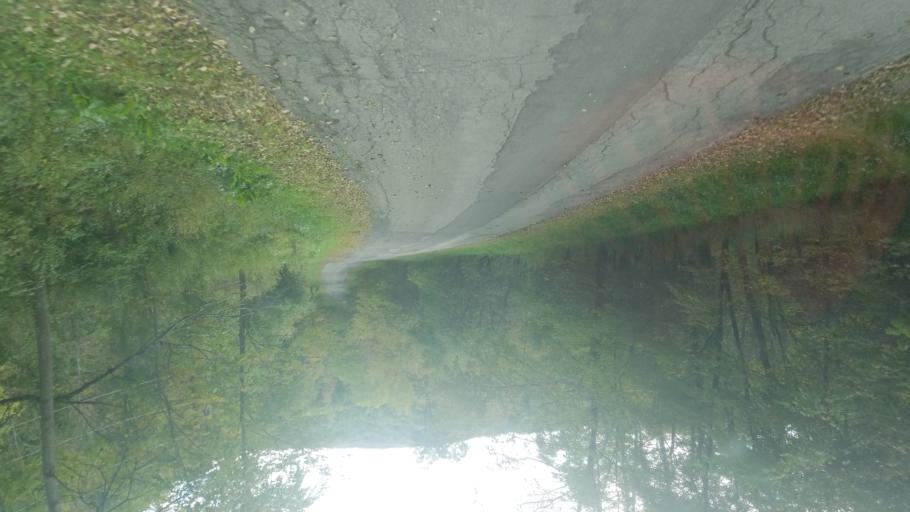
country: US
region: New York
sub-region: Allegany County
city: Cuba
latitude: 42.2250
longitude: -78.3431
